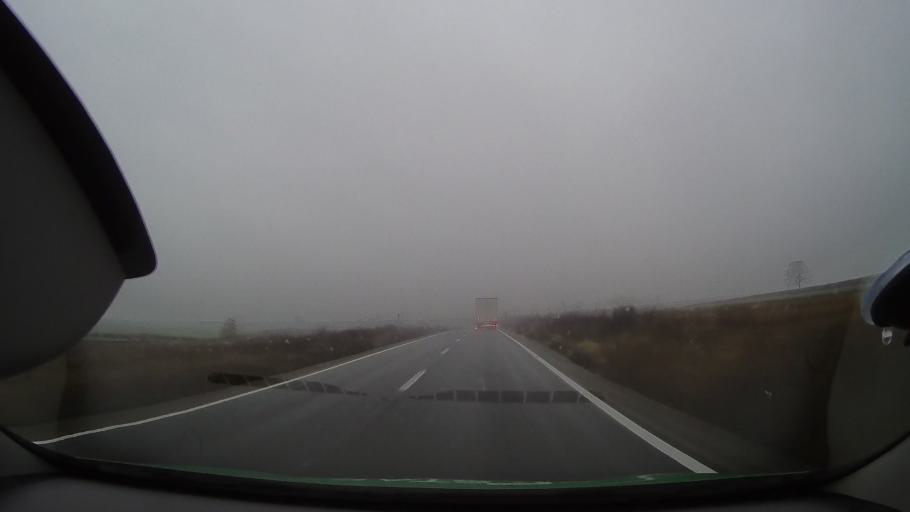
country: RO
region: Bihor
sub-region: Comuna Olcea
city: Olcea
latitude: 46.6740
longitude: 21.9650
